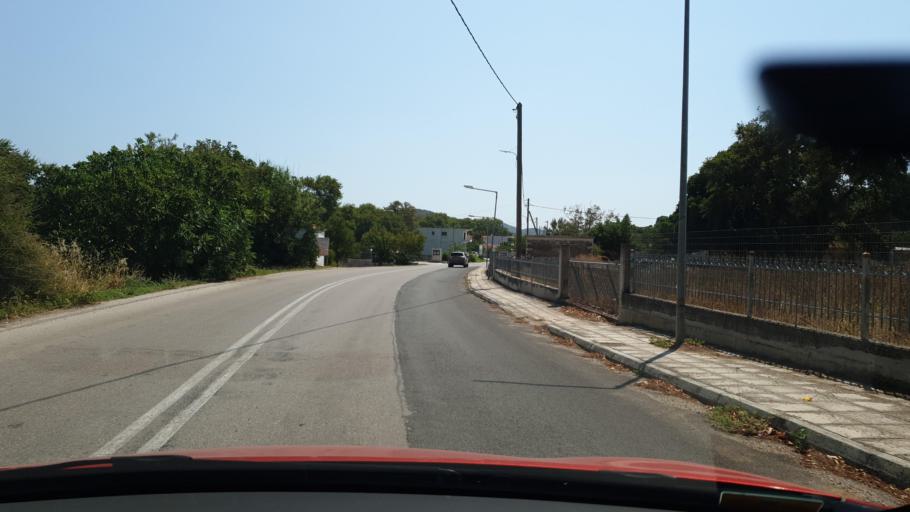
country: GR
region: Central Greece
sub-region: Nomos Evvoias
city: Aliveri
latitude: 38.4459
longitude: 24.1141
